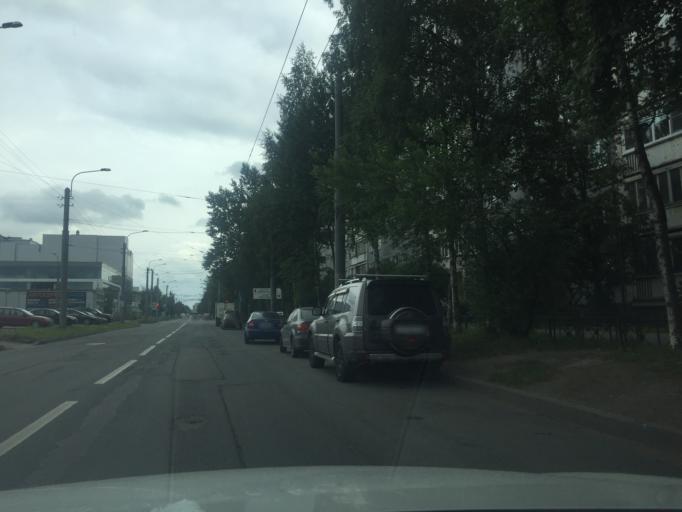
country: RU
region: Leningrad
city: Parnas
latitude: 60.0586
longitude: 30.3453
